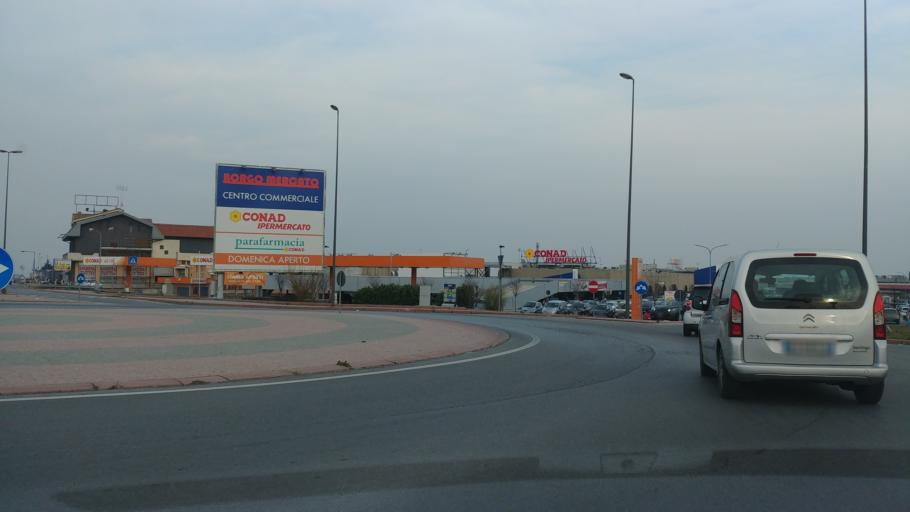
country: IT
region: Piedmont
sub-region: Provincia di Cuneo
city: Borgo San Dalmazzo
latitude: 44.3475
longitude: 7.5048
